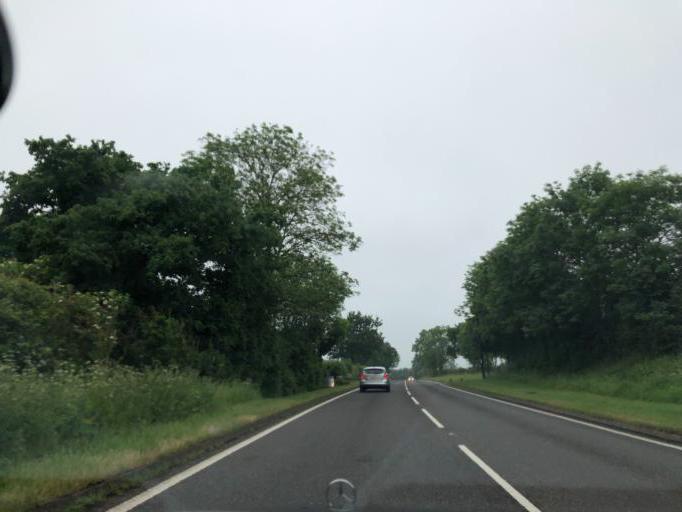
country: GB
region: England
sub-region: Warwickshire
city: Wellesbourne Mountford
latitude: 52.2269
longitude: -1.5363
